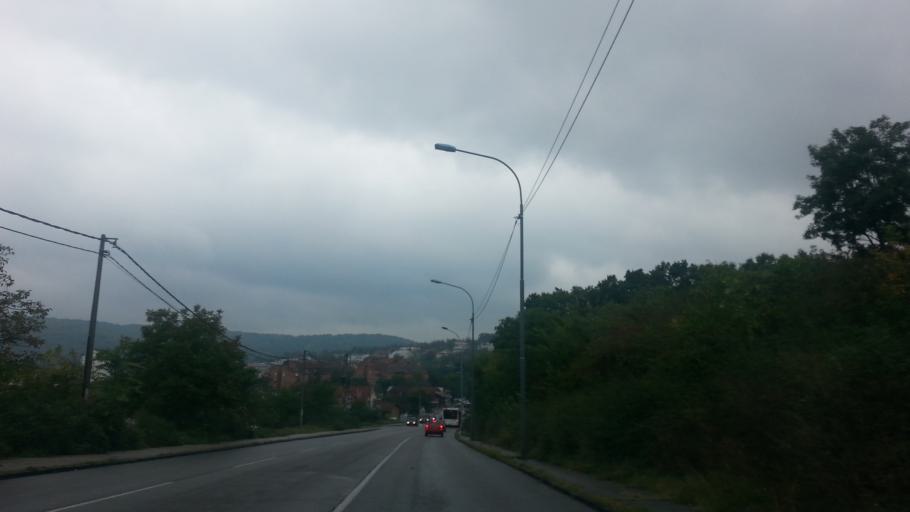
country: RS
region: Central Serbia
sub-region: Belgrade
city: Savski Venac
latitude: 44.7562
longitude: 20.4636
